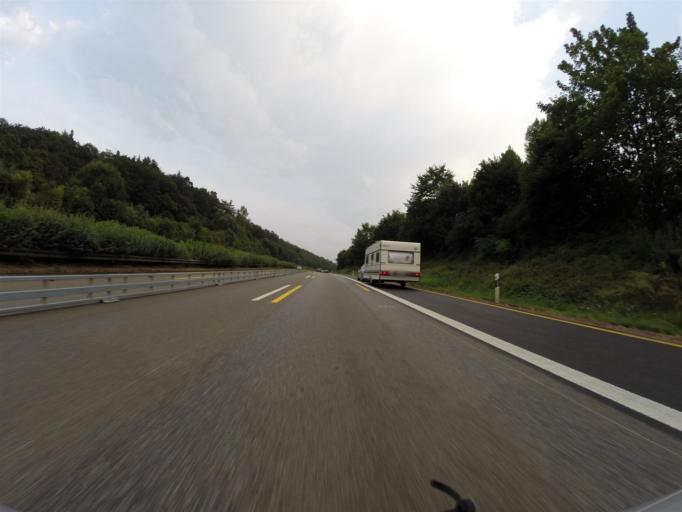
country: DE
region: Hesse
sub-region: Regierungsbezirk Kassel
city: Homberg
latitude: 50.9951
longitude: 9.4737
